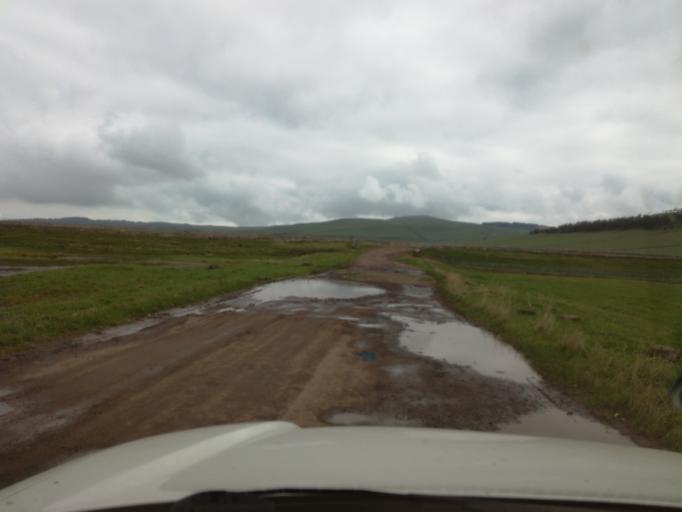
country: AM
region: Lorri
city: Metsavan
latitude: 41.1960
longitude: 44.1977
